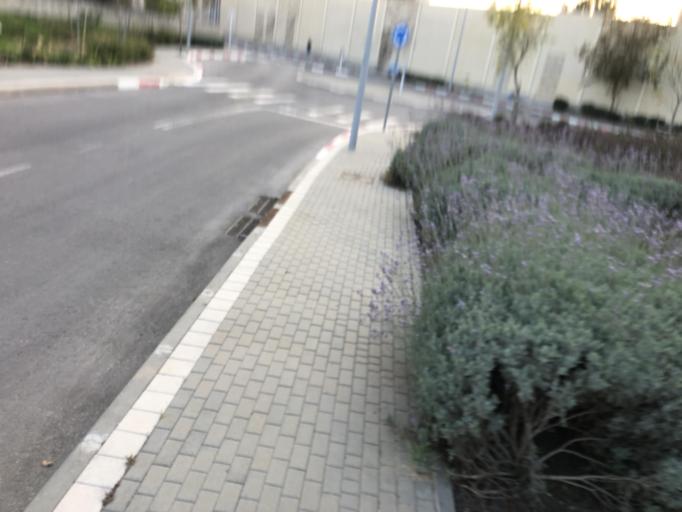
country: IL
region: Northern District
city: `Akko
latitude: 32.9288
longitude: 35.0837
